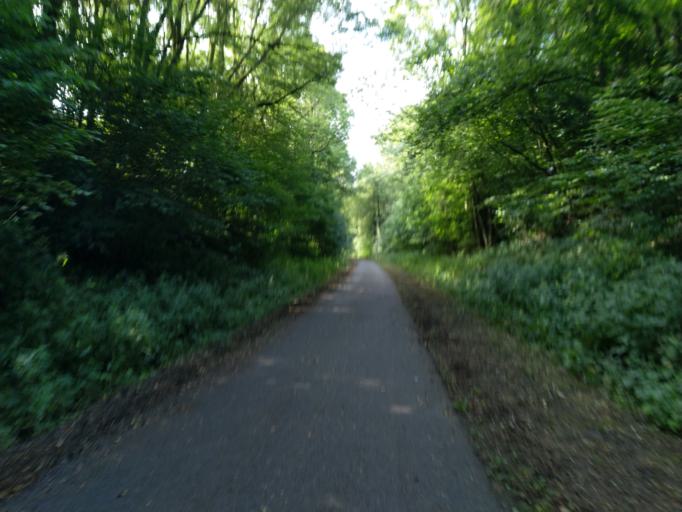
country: BE
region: Wallonia
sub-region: Province du Hainaut
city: Erquelinnes
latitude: 50.3210
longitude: 4.1001
